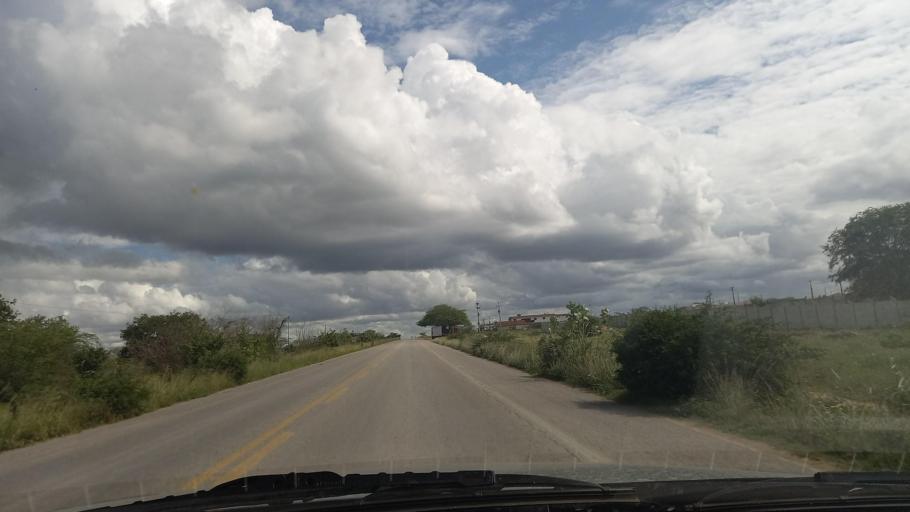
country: BR
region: Pernambuco
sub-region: Cachoeirinha
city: Cachoeirinha
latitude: -8.4956
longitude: -36.2395
